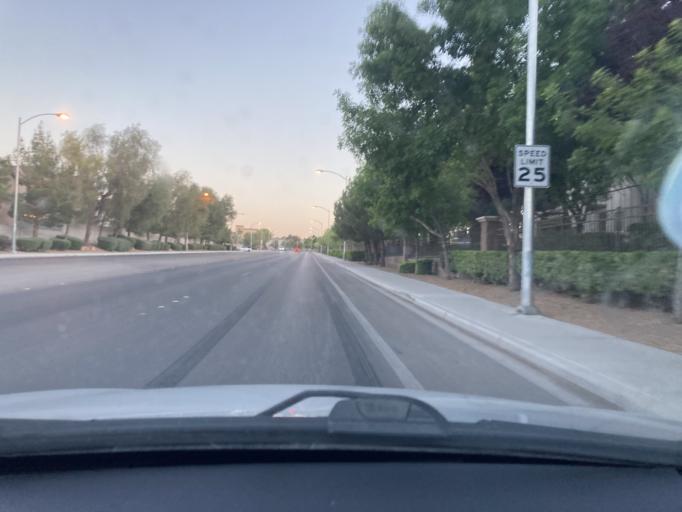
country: US
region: Nevada
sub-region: Clark County
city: Enterprise
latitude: 36.0583
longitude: -115.2883
